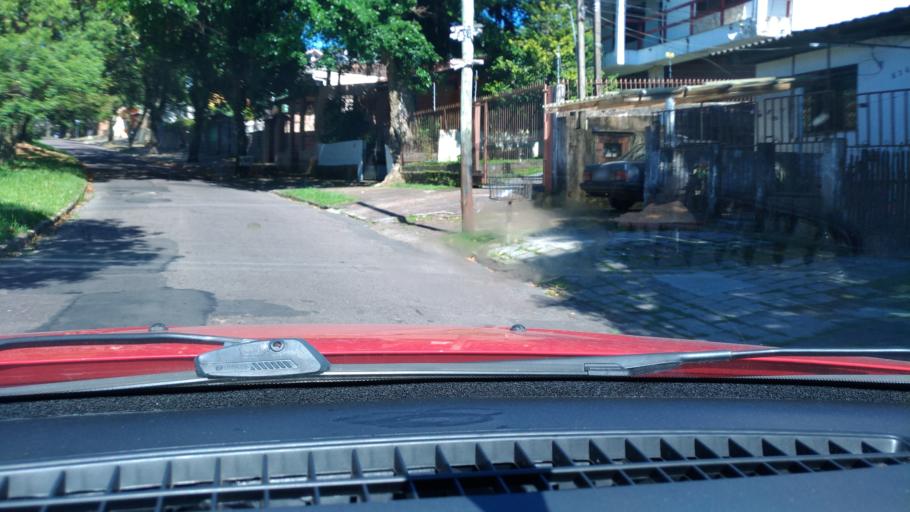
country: BR
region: Rio Grande do Sul
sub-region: Cachoeirinha
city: Cachoeirinha
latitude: -30.0324
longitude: -51.1285
